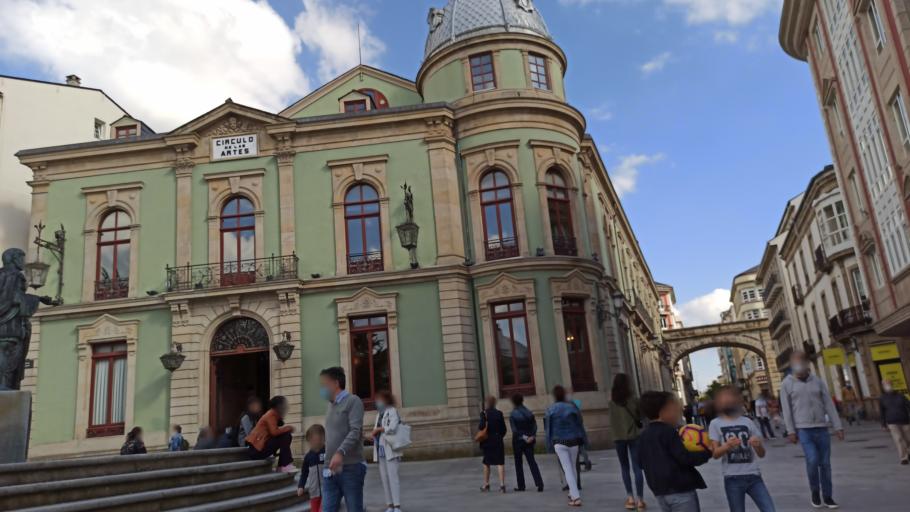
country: ES
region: Galicia
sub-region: Provincia de Lugo
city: Lugo
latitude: 43.0094
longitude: -7.5572
